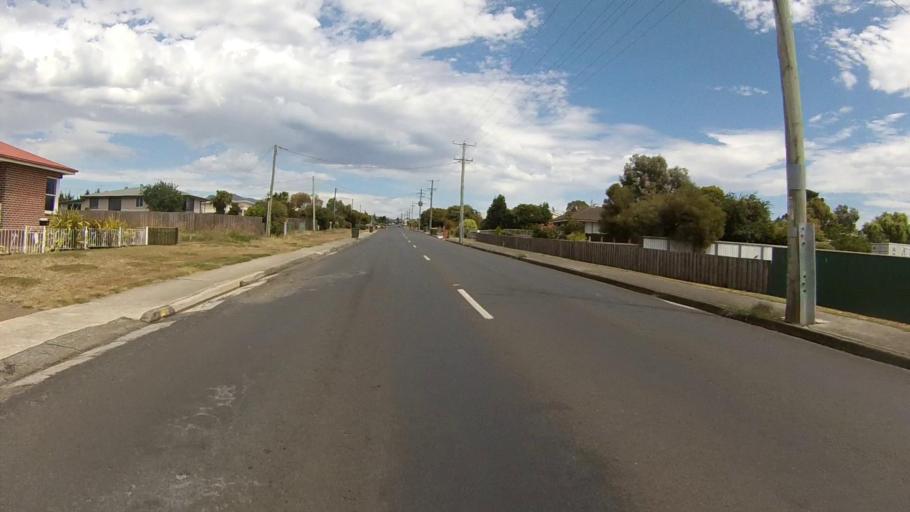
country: AU
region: Tasmania
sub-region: Brighton
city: Bridgewater
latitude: -42.7011
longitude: 147.2580
